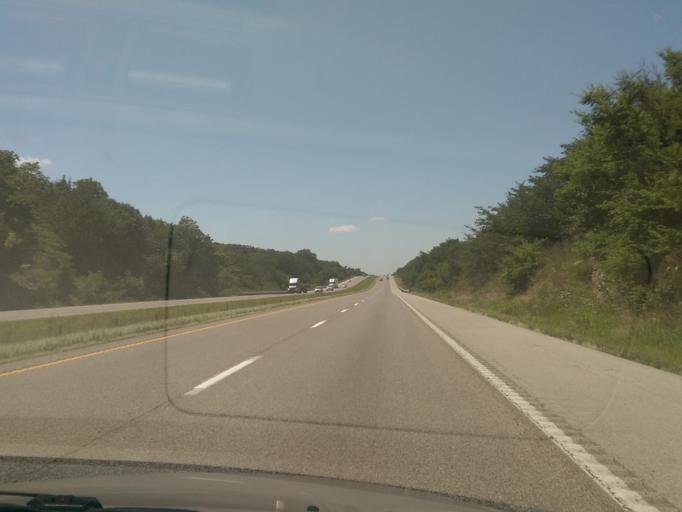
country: US
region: Missouri
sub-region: Saline County
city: Marshall
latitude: 38.9552
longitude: -93.1181
